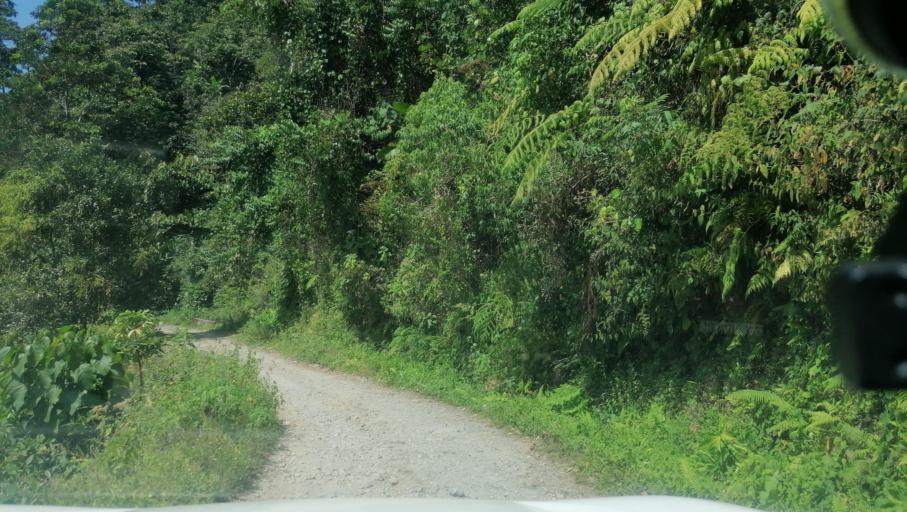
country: MX
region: Chiapas
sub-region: Union Juarez
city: Santo Domingo
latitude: 15.0760
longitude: -92.1298
